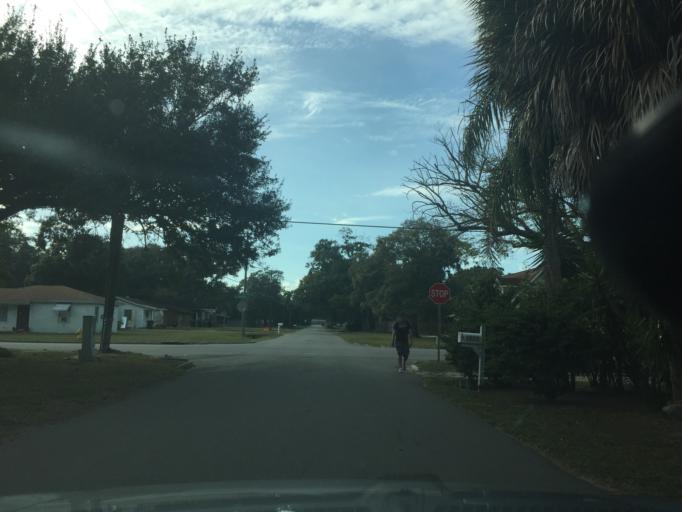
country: US
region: Florida
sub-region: Hillsborough County
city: Tampa
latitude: 27.9459
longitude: -82.4971
